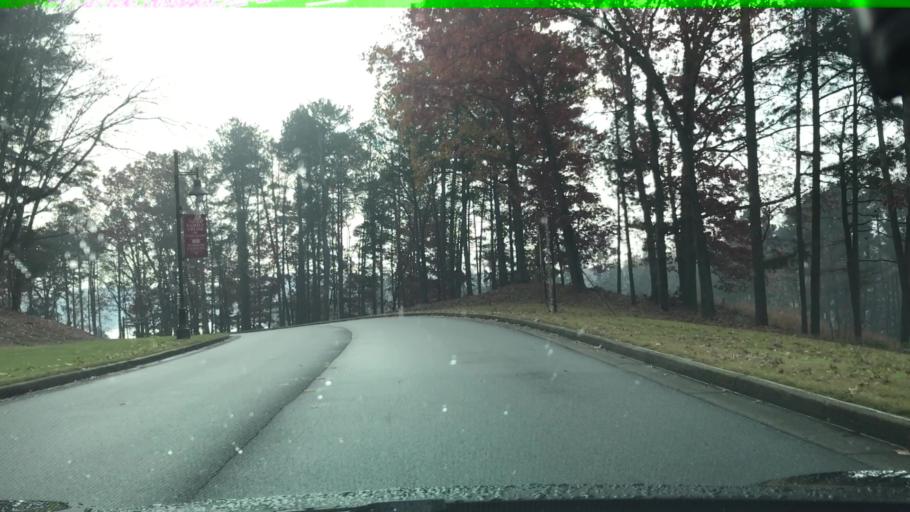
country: US
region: Georgia
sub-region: Gwinnett County
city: Buford
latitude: 34.1768
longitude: -84.0205
